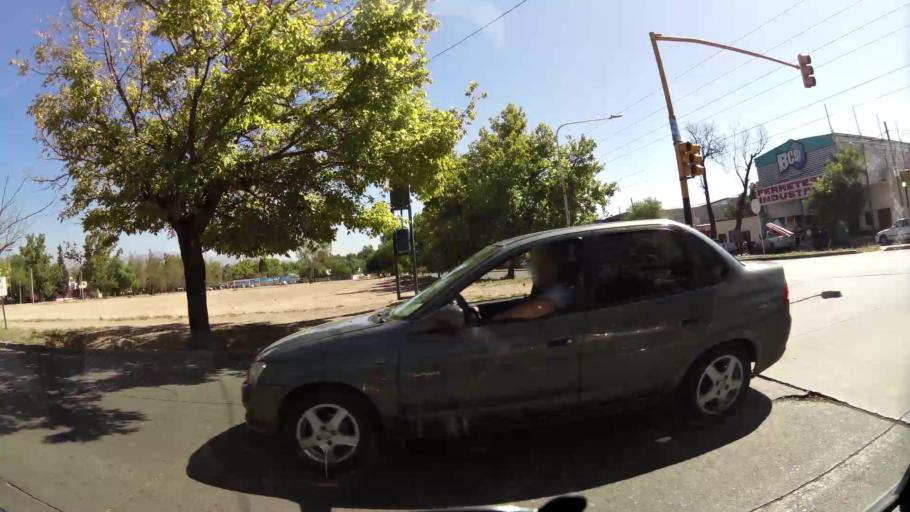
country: AR
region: Mendoza
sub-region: Departamento de Godoy Cruz
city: Godoy Cruz
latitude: -32.9068
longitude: -68.8653
